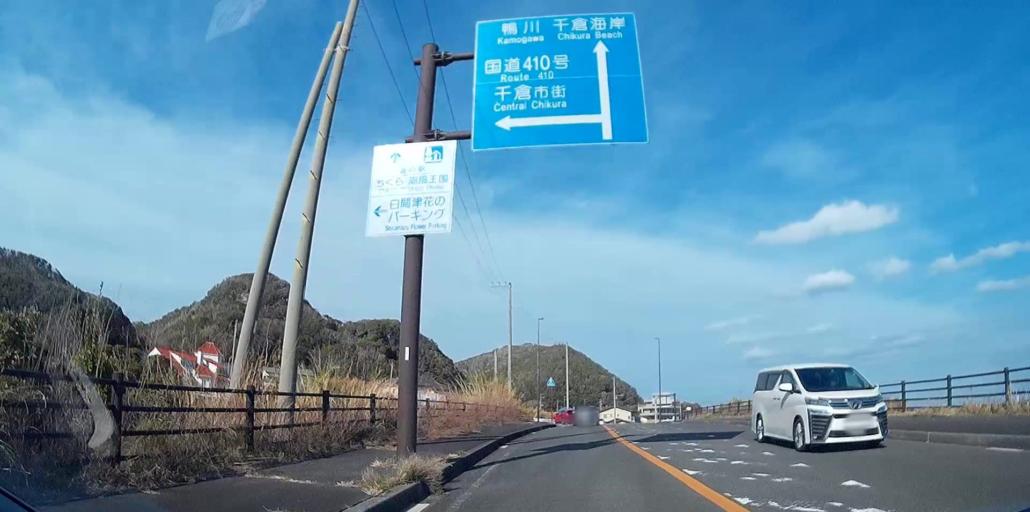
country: JP
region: Chiba
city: Tateyama
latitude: 34.9138
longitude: 139.9317
